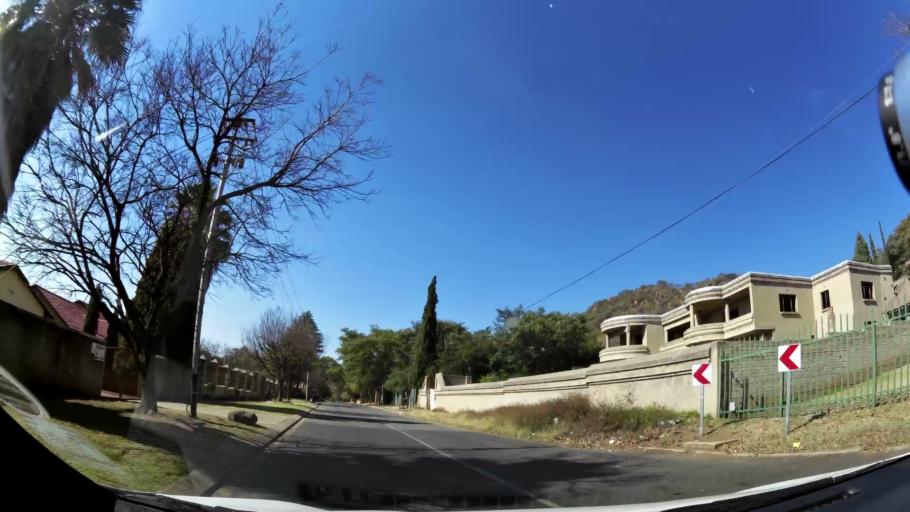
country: ZA
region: Gauteng
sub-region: City of Johannesburg Metropolitan Municipality
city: Johannesburg
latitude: -26.2793
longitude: 27.9947
